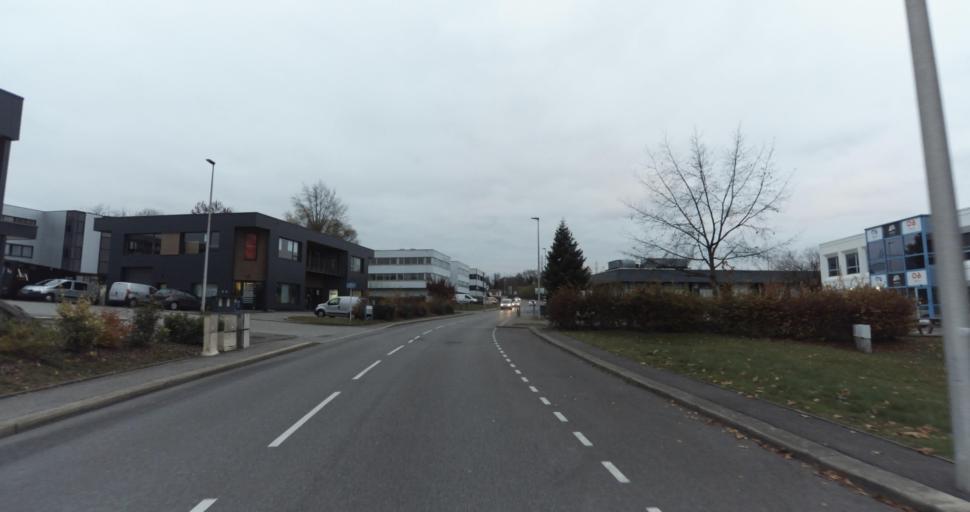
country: FR
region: Rhone-Alpes
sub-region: Departement de la Haute-Savoie
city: Seynod
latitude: 45.8929
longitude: 6.0881
